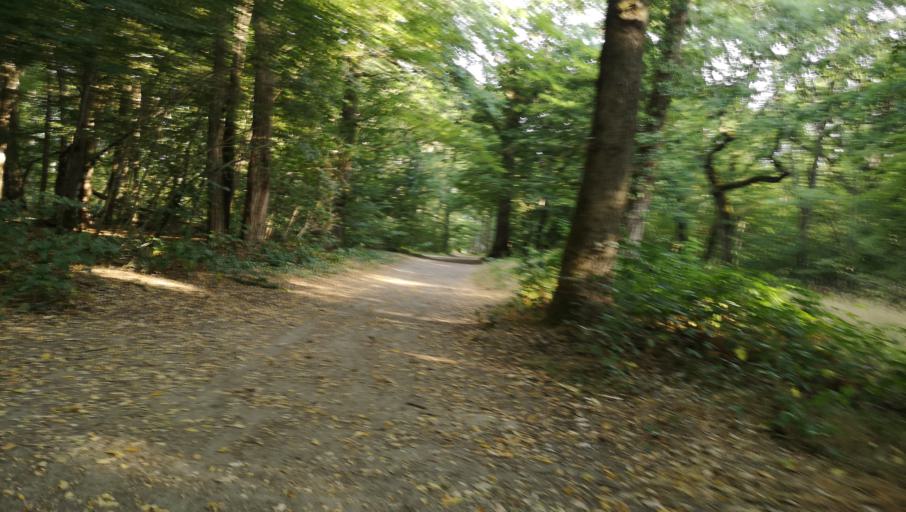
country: FR
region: Centre
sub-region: Departement du Loiret
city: Boigny-sur-Bionne
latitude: 47.9368
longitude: 1.9980
